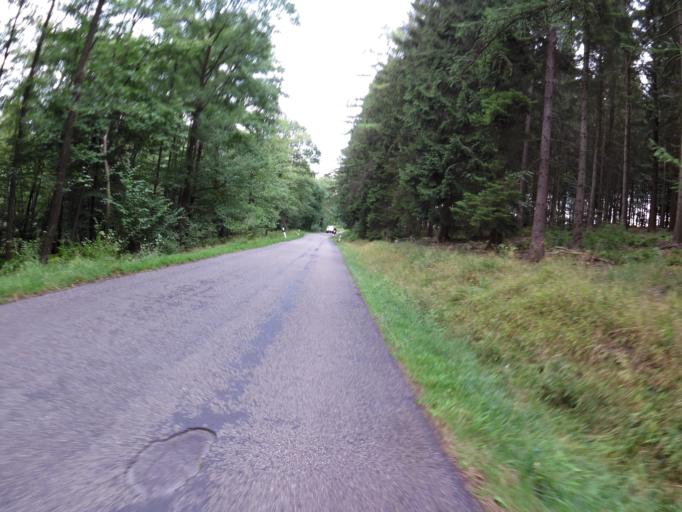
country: DE
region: North Rhine-Westphalia
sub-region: Regierungsbezirk Koln
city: Hurtgenwald
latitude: 50.7562
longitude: 6.3171
